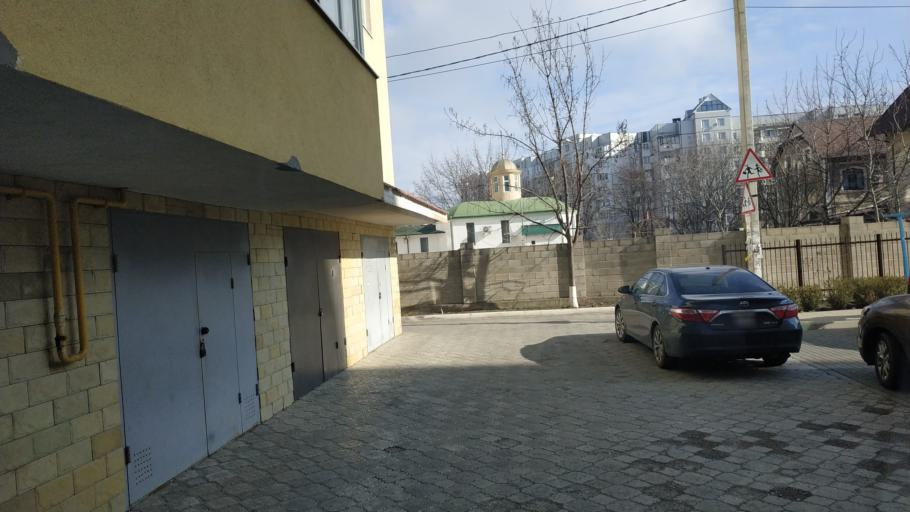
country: MD
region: Chisinau
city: Vatra
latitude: 47.0399
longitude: 28.7645
